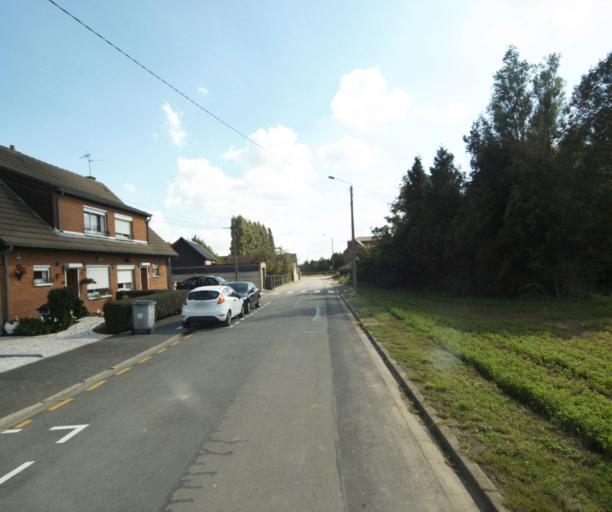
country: FR
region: Nord-Pas-de-Calais
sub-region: Departement du Nord
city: Illies
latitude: 50.5612
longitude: 2.8387
